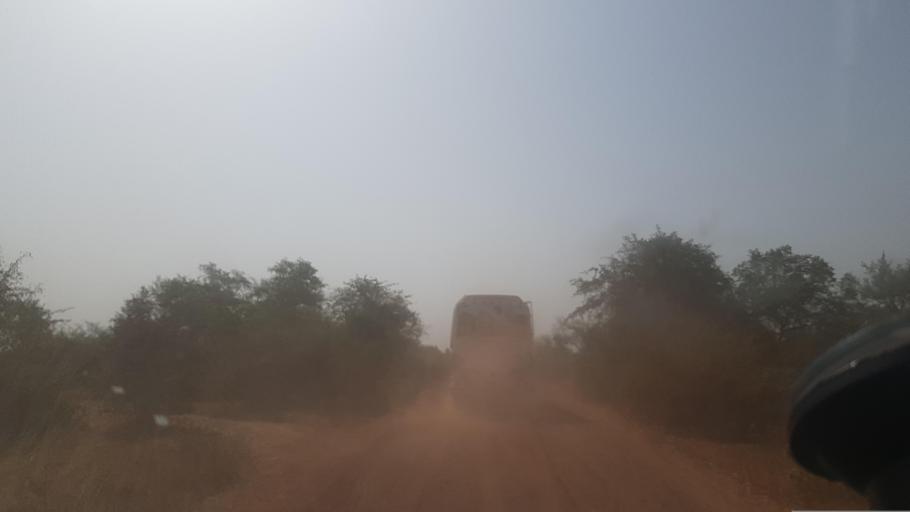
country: ML
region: Segou
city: Baroueli
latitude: 13.0723
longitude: -6.4803
